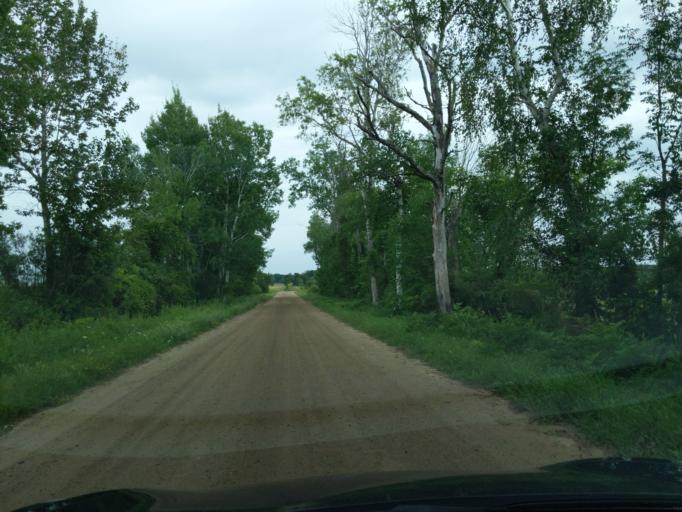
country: US
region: Michigan
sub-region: Clare County
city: Harrison
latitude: 43.9878
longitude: -85.0009
